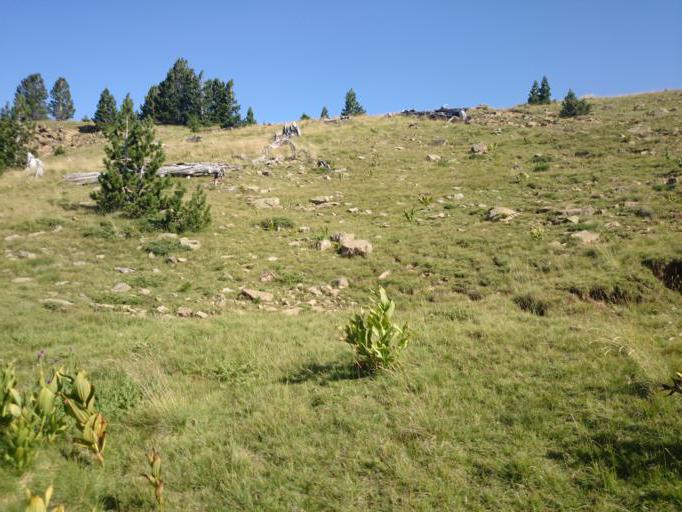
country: AL
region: Elbasan
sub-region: Rrethi i Gramshit
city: Lenias
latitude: 40.8207
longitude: 20.4671
